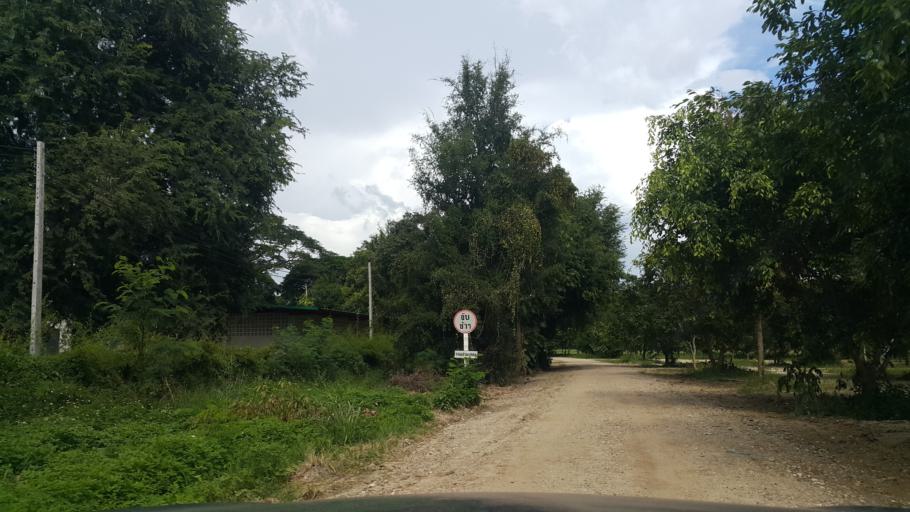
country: TH
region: Chiang Mai
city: Chiang Mai
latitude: 18.8330
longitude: 98.9966
